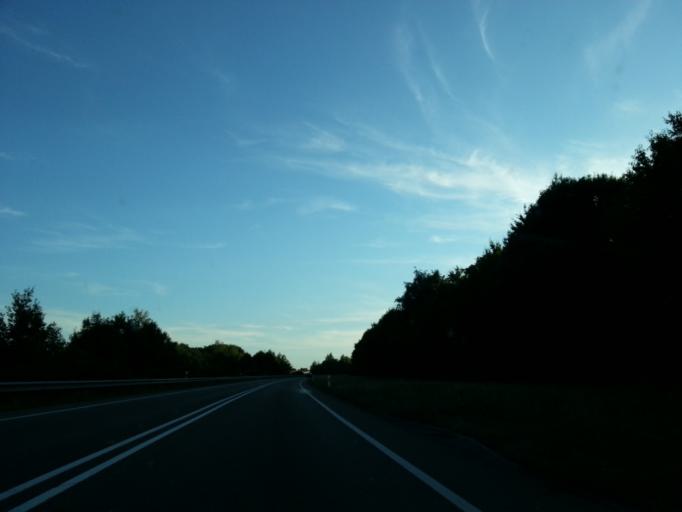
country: DE
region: Rheinland-Pfalz
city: Thaleischweiler-Froschen
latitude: 49.2491
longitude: 7.5844
